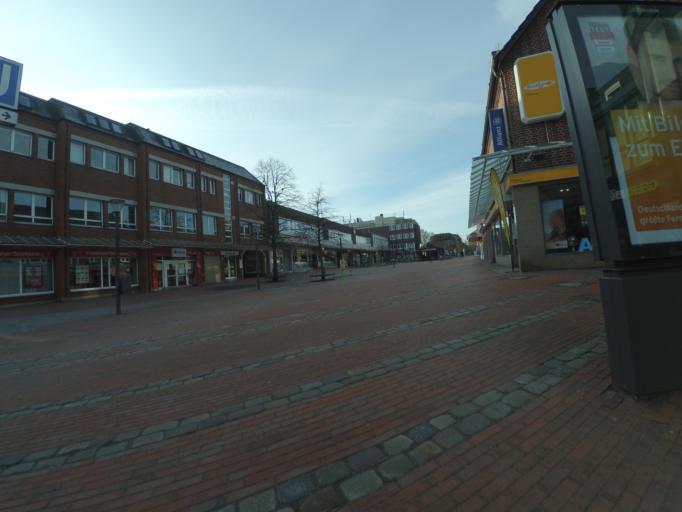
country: DE
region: Hamburg
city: Stellingen
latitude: 53.6220
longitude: 9.9522
